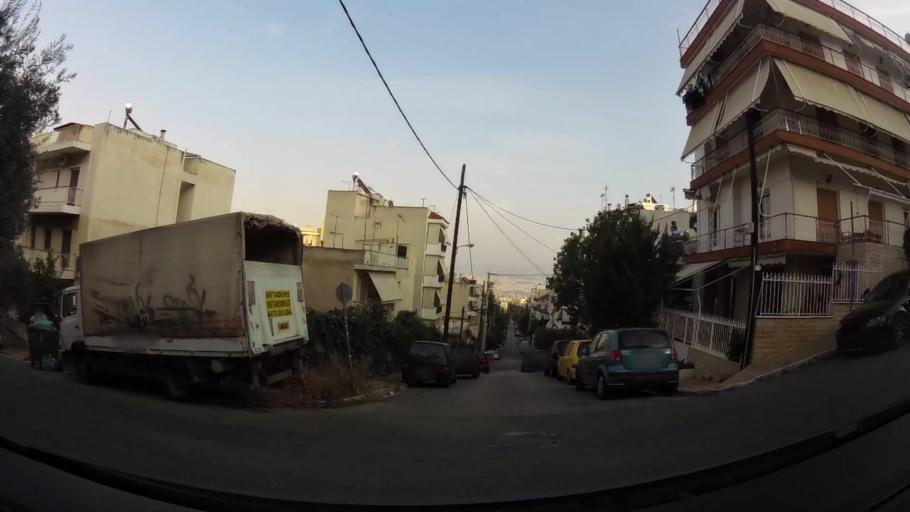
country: GR
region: Attica
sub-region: Nomarchia Athinas
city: Petroupolis
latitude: 38.0420
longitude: 23.6728
